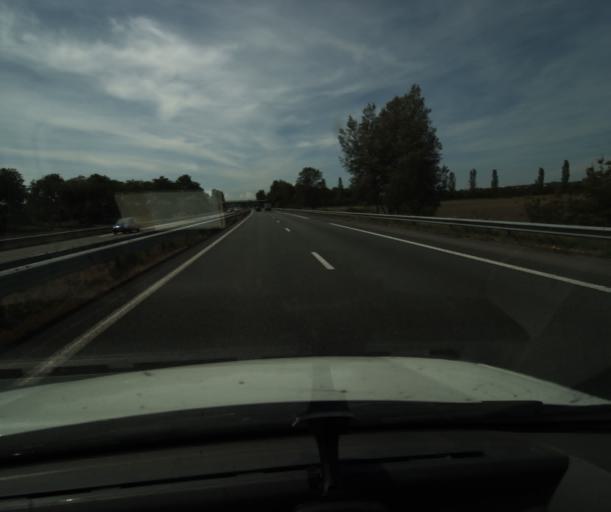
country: FR
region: Languedoc-Roussillon
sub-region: Departement de l'Aude
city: Castelnaudary
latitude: 43.2831
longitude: 1.9764
